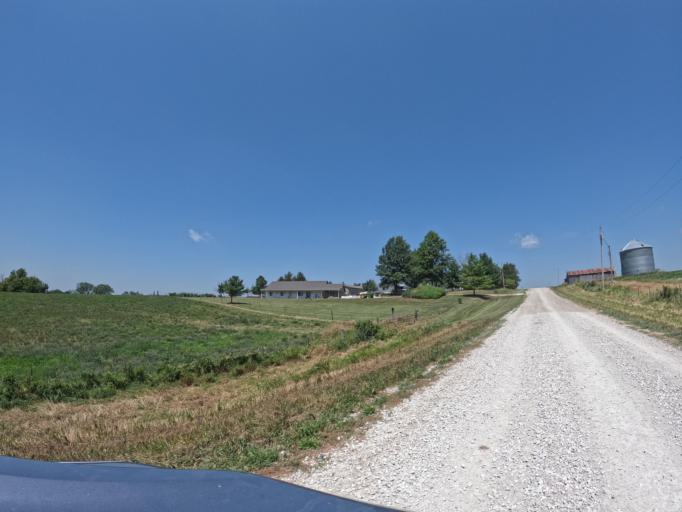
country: US
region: Iowa
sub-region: Keokuk County
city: Sigourney
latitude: 41.2596
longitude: -92.1697
